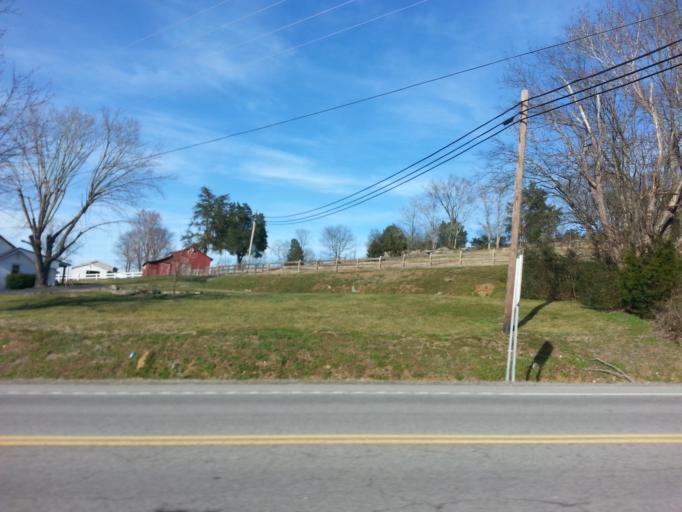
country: US
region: Tennessee
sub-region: Cannon County
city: Woodbury
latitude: 35.8206
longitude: -86.0475
